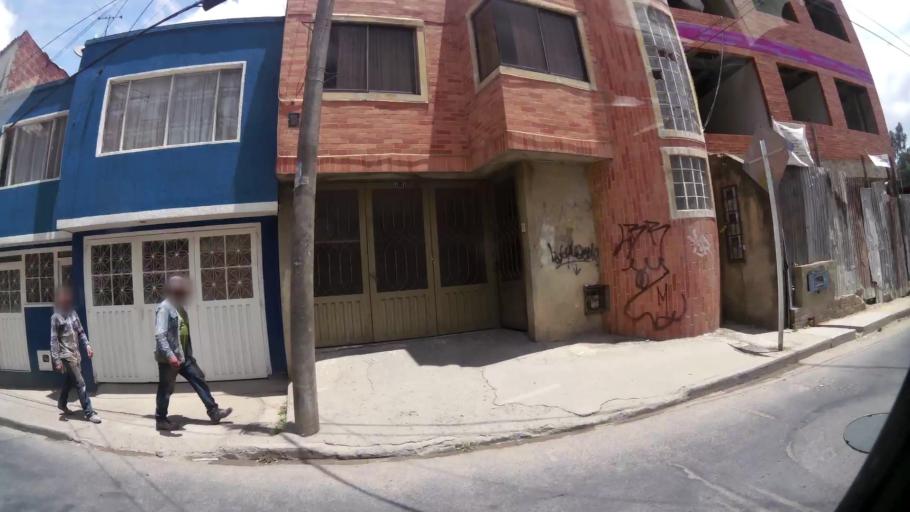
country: CO
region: Cundinamarca
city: Cota
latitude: 4.7379
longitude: -74.0772
